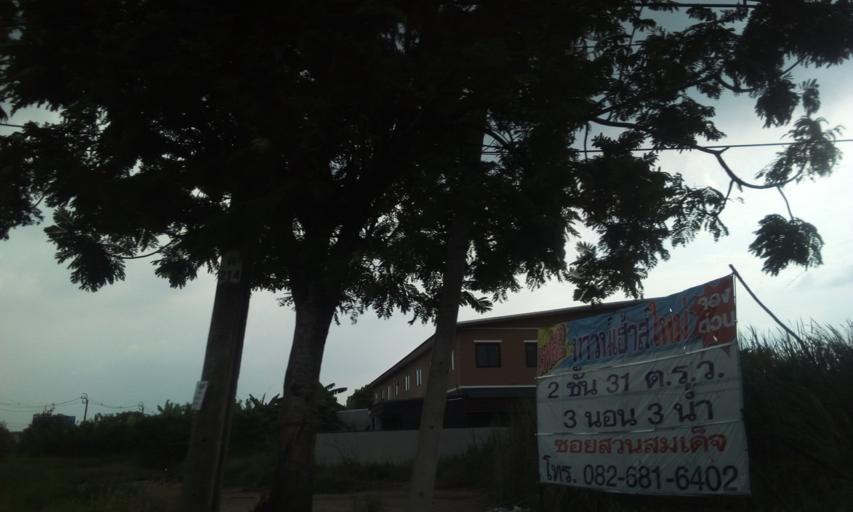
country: TH
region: Bangkok
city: Don Mueang
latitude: 13.9374
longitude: 100.5565
